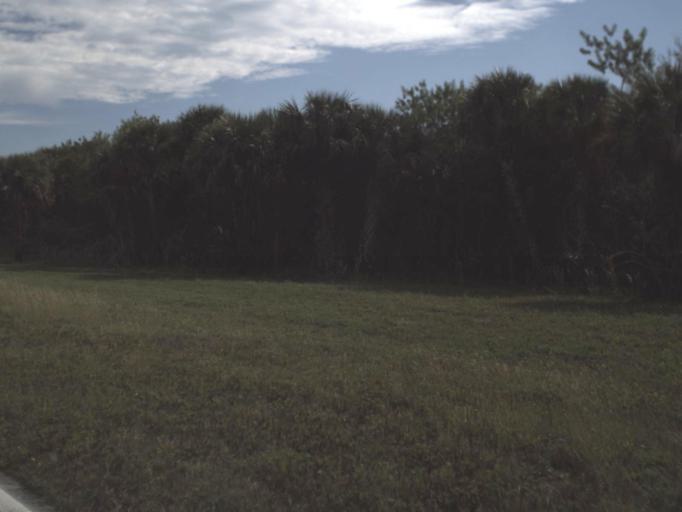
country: US
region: Florida
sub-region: Brevard County
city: Merritt Island
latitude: 28.5263
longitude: -80.7188
